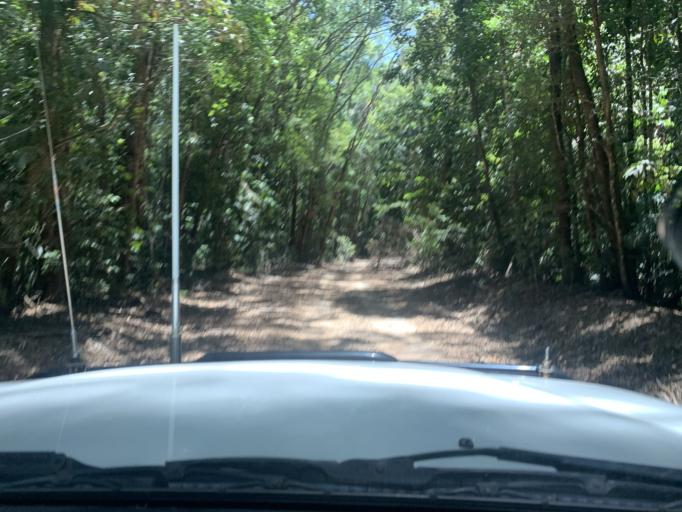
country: AU
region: Queensland
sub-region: Cairns
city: Redlynch
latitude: -16.9409
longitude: 145.6261
